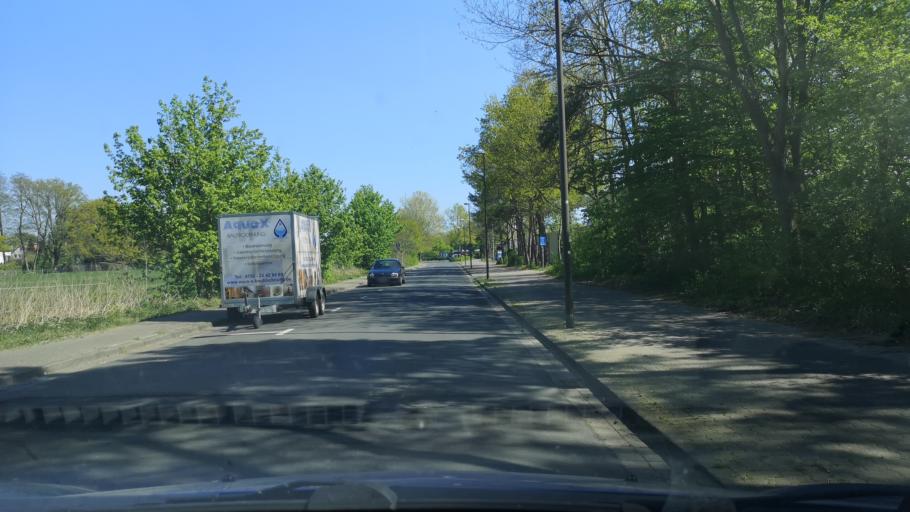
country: DE
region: Lower Saxony
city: Langenhagen
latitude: 52.4492
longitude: 9.7456
